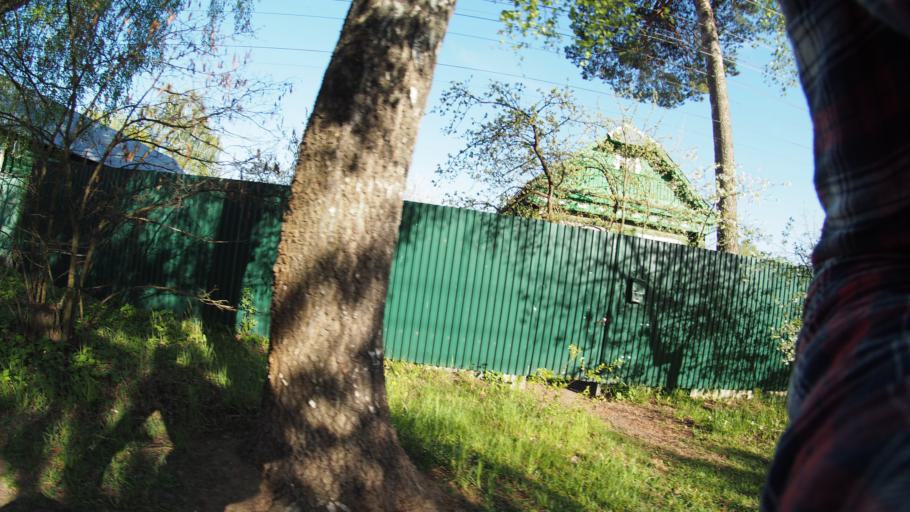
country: RU
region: Moskovskaya
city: Ramenskoye
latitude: 55.5590
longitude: 38.1988
